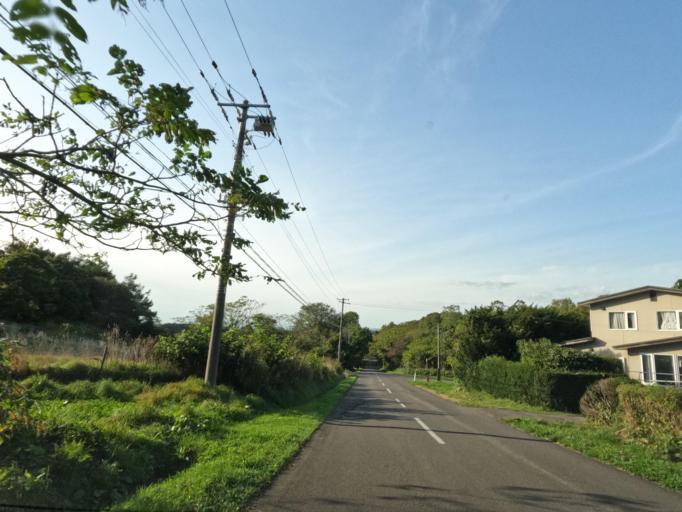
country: JP
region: Hokkaido
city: Date
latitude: 42.4114
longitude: 140.9153
